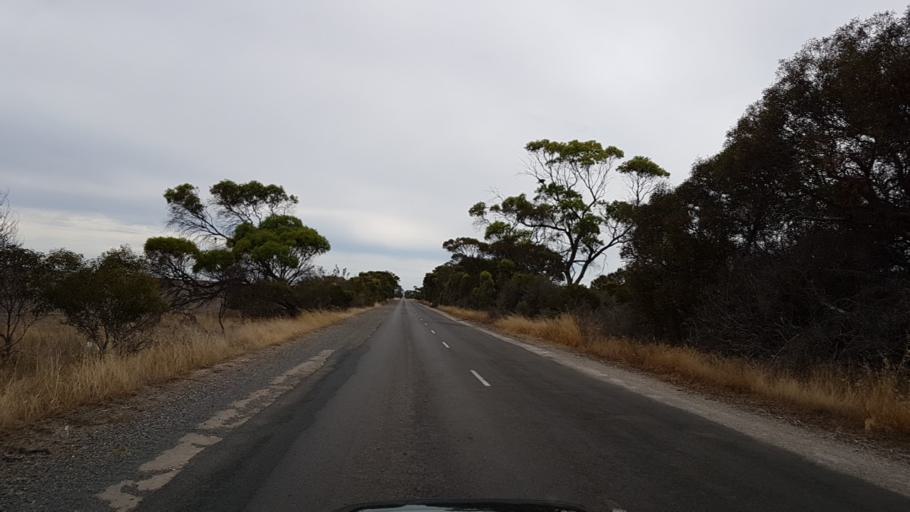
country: AU
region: South Australia
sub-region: Yorke Peninsula
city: Honiton
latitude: -34.9850
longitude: 137.1674
